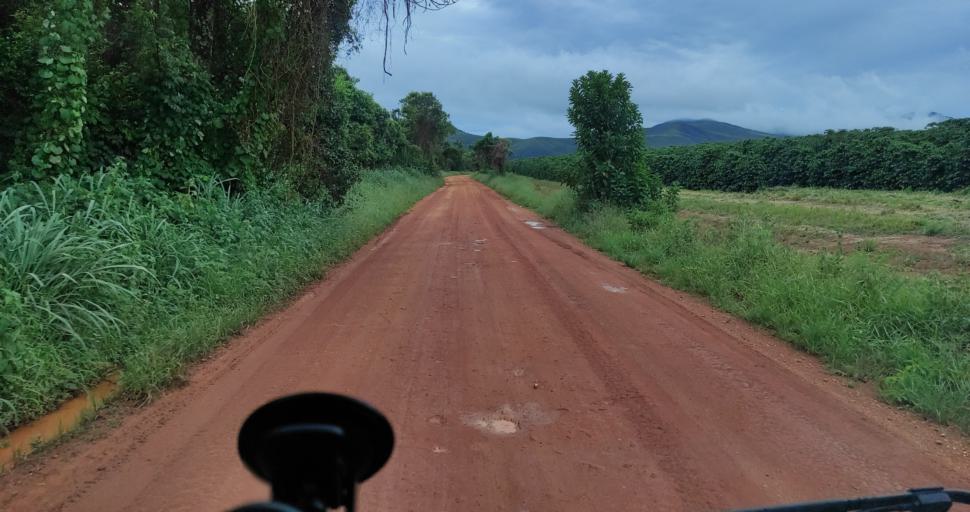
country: BR
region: Minas Gerais
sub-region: Piui
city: Piui
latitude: -20.2813
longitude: -46.3623
